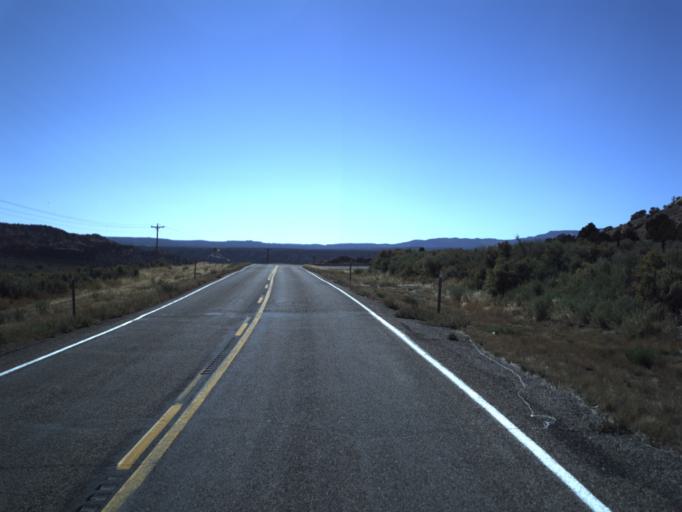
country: US
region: Utah
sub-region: Garfield County
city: Panguitch
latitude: 37.5607
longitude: -112.0156
